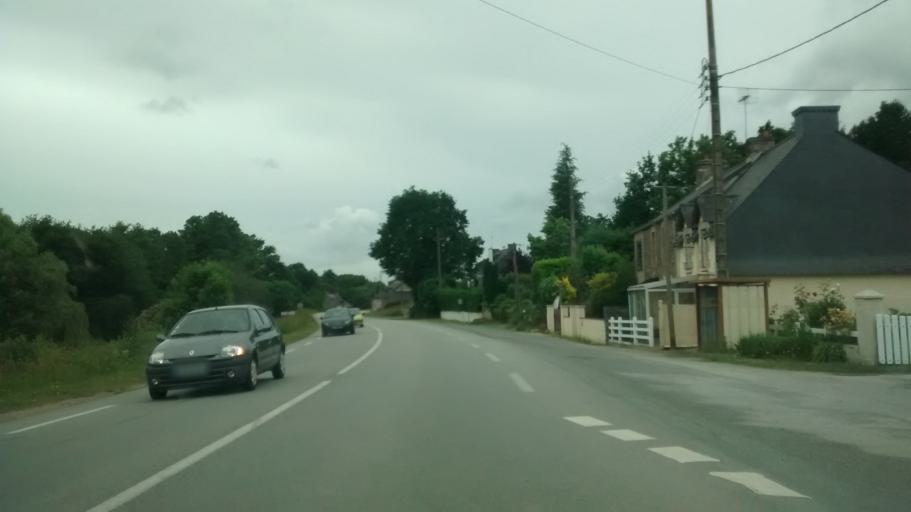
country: FR
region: Brittany
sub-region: Departement du Morbihan
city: Malestroit
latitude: 47.8110
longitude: -2.3530
